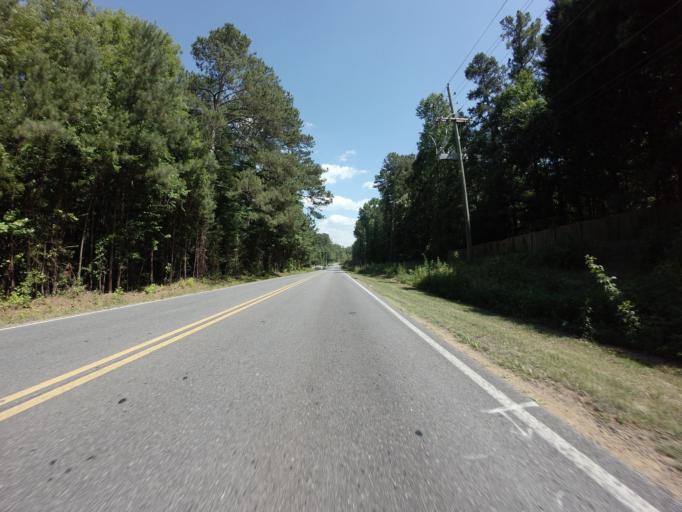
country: US
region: Georgia
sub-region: Fulton County
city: Johns Creek
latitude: 34.0758
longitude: -84.1819
